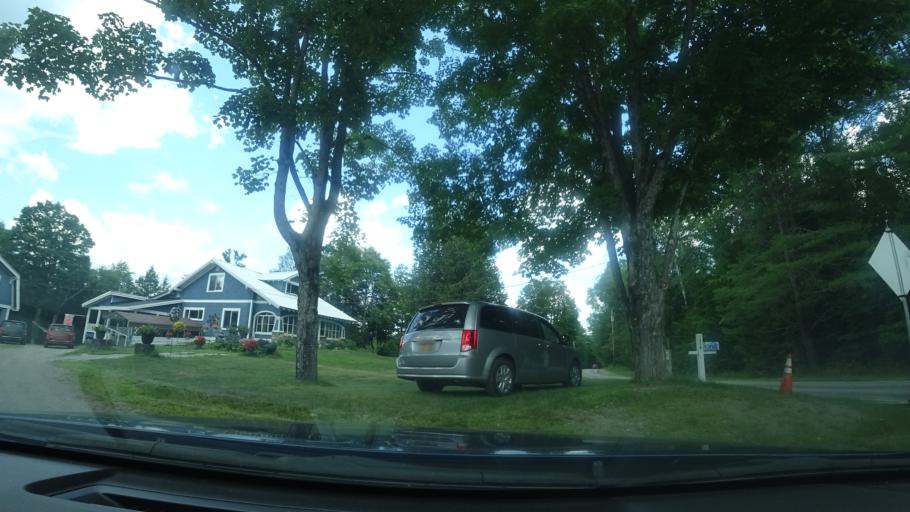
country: US
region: New York
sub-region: Warren County
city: Warrensburg
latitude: 43.6546
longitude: -73.8332
